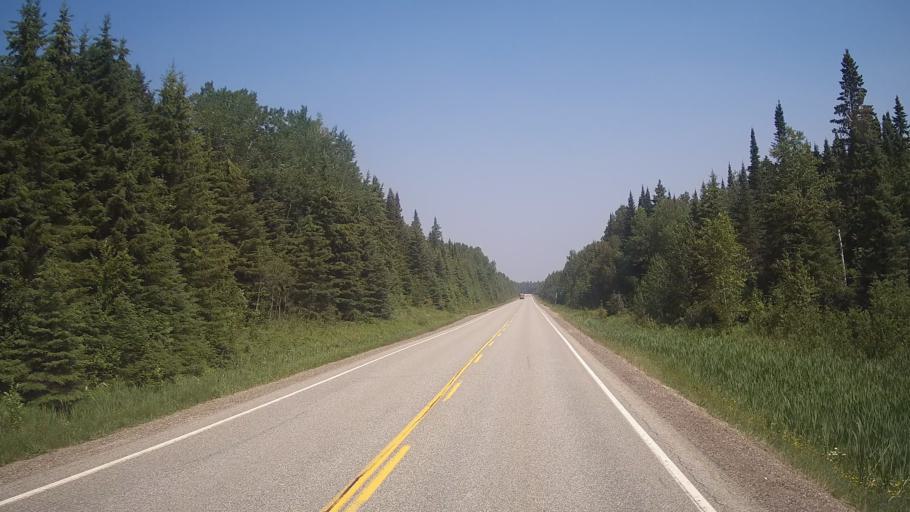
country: CA
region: Ontario
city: Timmins
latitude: 48.2062
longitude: -81.5767
